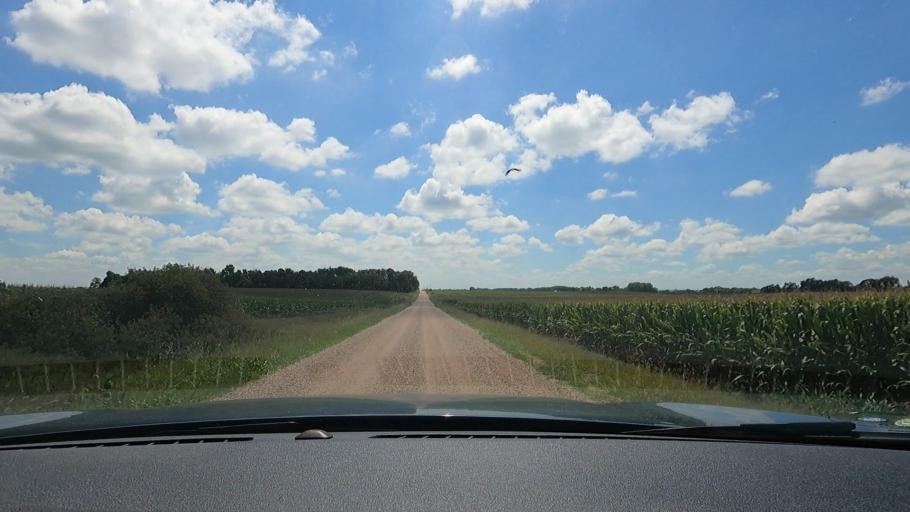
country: US
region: Nebraska
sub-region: Saunders County
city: Wahoo
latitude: 41.2685
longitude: -96.5420
